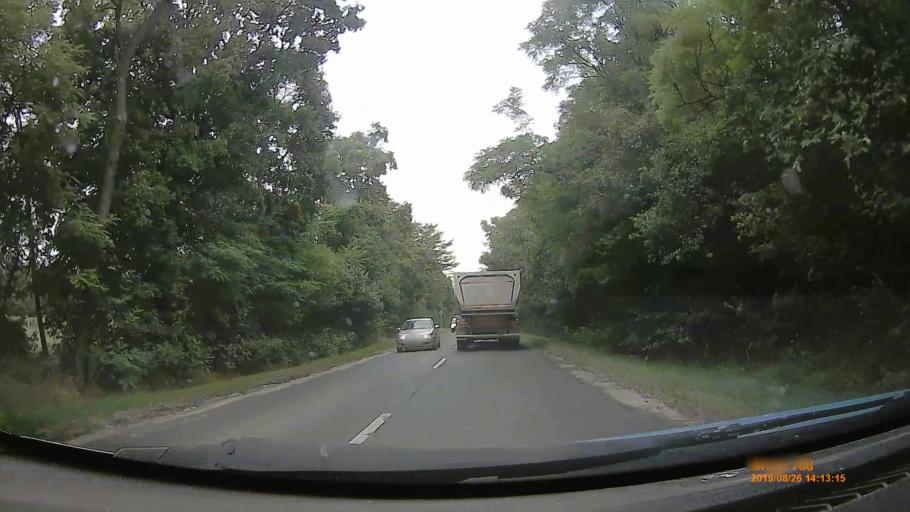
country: HU
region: Fejer
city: Csakvar
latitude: 47.4337
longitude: 18.5316
